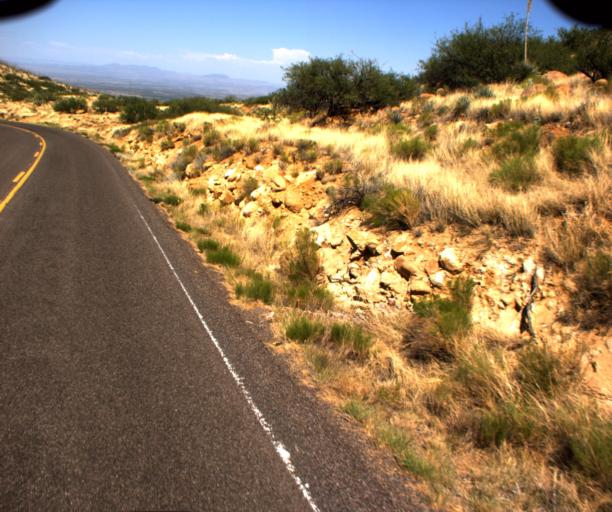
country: US
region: Arizona
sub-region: Graham County
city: Swift Trail Junction
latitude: 32.6861
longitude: -109.7658
